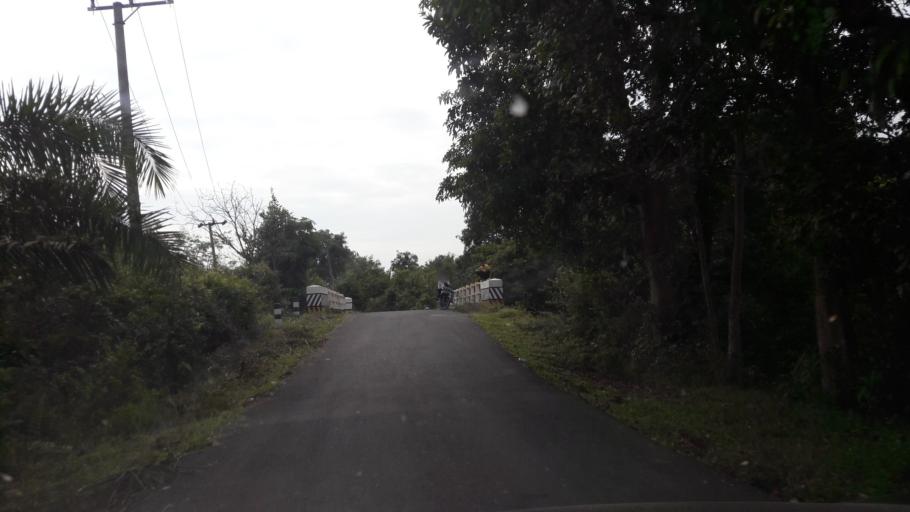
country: ID
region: South Sumatra
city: Gunungmenang
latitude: -3.0988
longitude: 104.0487
